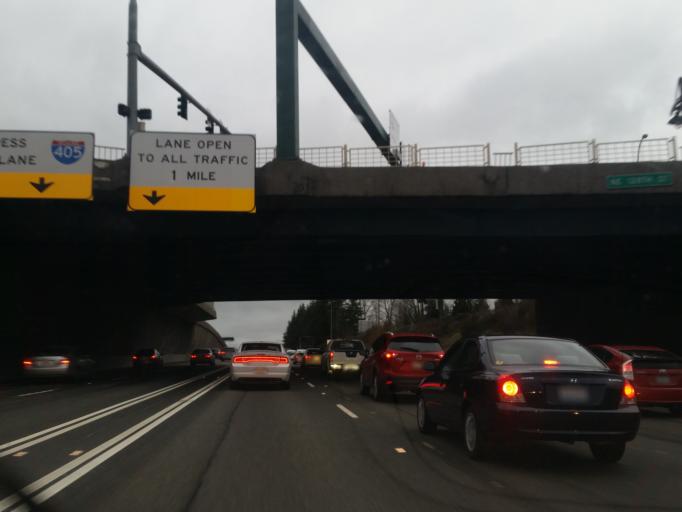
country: US
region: Washington
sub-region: King County
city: Kingsgate
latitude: 47.7145
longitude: -122.1849
